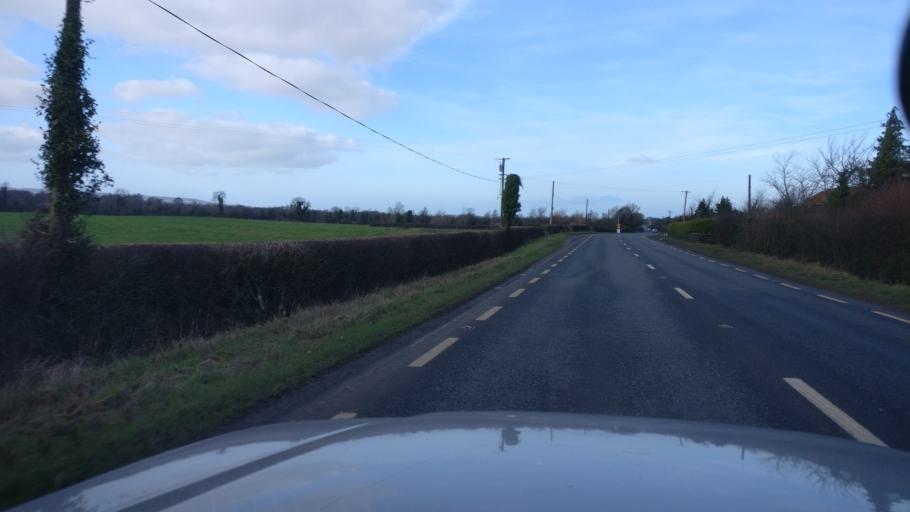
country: IE
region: Leinster
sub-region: Laois
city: Portlaoise
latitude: 53.0582
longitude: -7.3239
